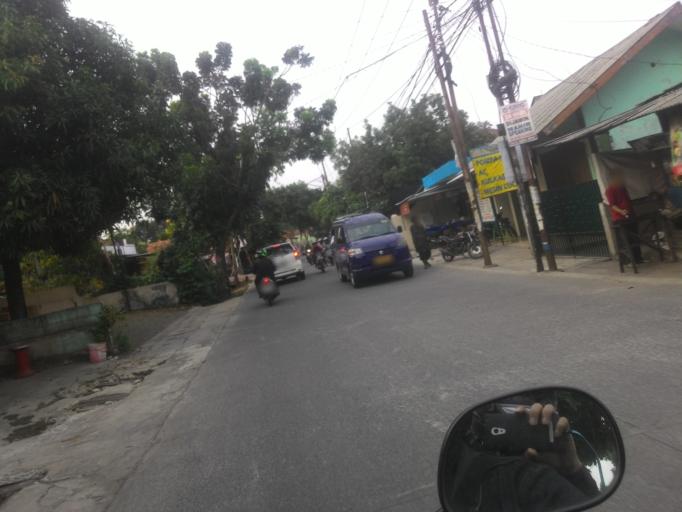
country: ID
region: West Java
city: Depok
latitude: -6.3615
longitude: 106.8165
